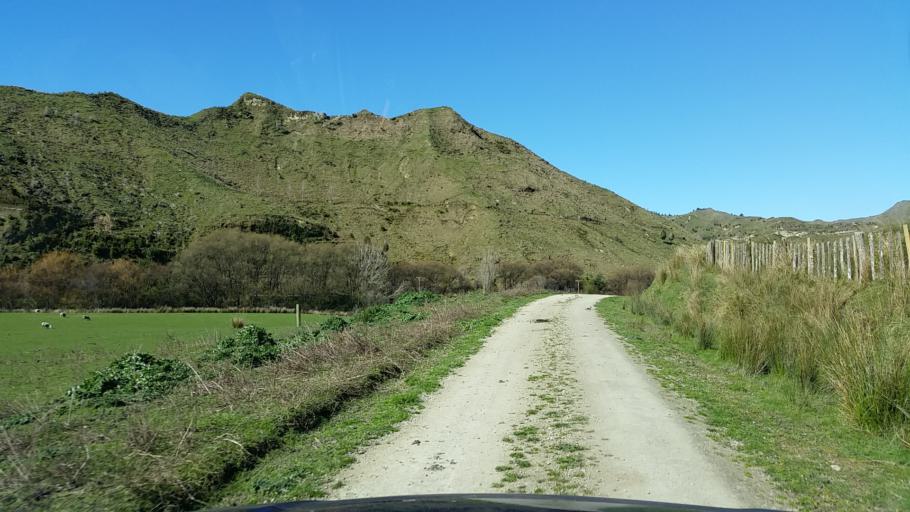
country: NZ
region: Manawatu-Wanganui
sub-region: Wanganui District
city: Wanganui
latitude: -39.6707
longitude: 174.8591
